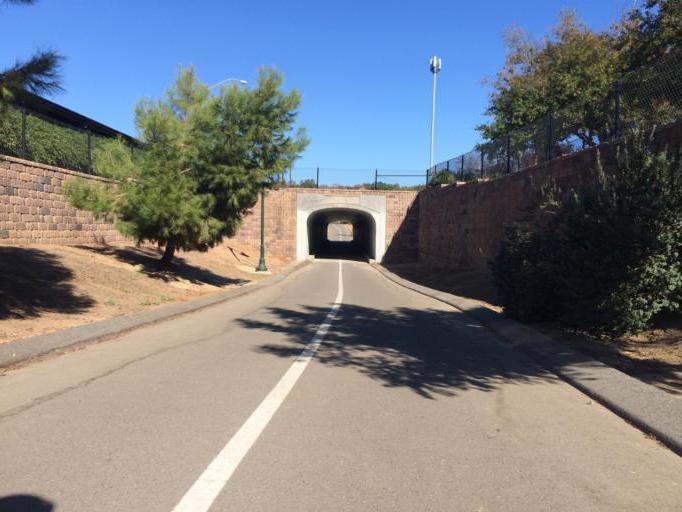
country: US
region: California
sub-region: Fresno County
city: Clovis
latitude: 36.8540
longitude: -119.7845
